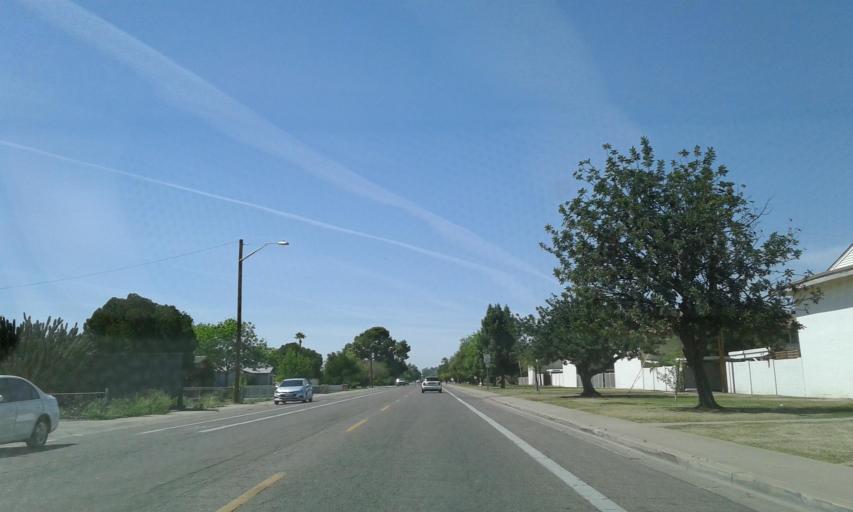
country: US
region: Arizona
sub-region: Maricopa County
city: Phoenix
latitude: 33.5022
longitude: -112.0919
